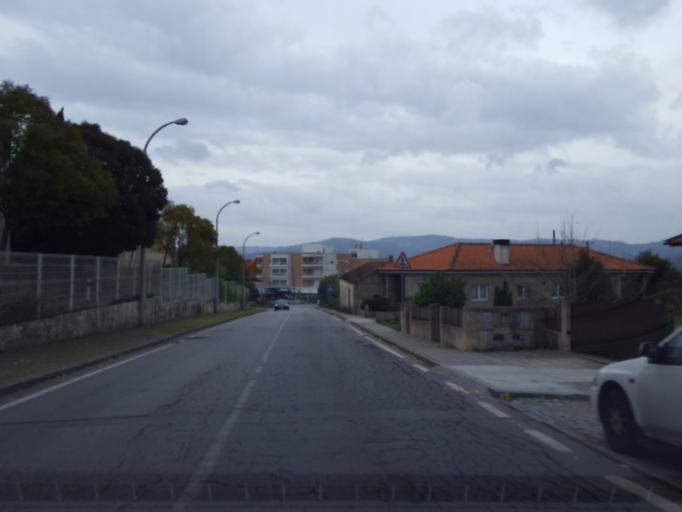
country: PT
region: Porto
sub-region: Marco de Canaveses
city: Marco de Canavezes
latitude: 41.1788
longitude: -8.1506
